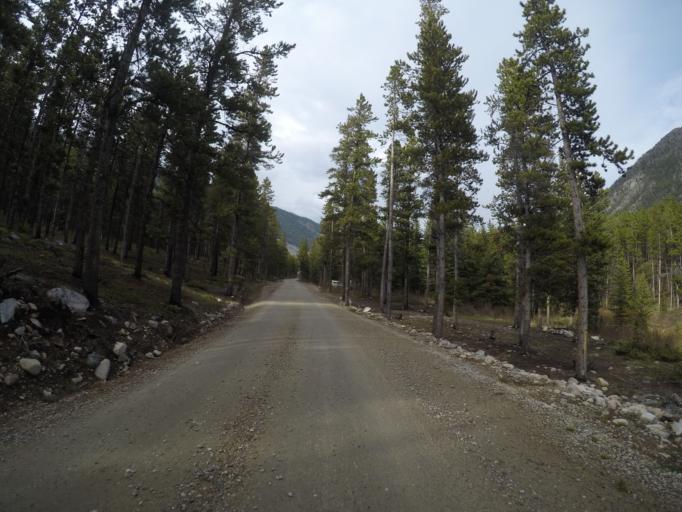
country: US
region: Montana
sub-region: Carbon County
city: Red Lodge
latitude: 45.0485
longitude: -109.4238
